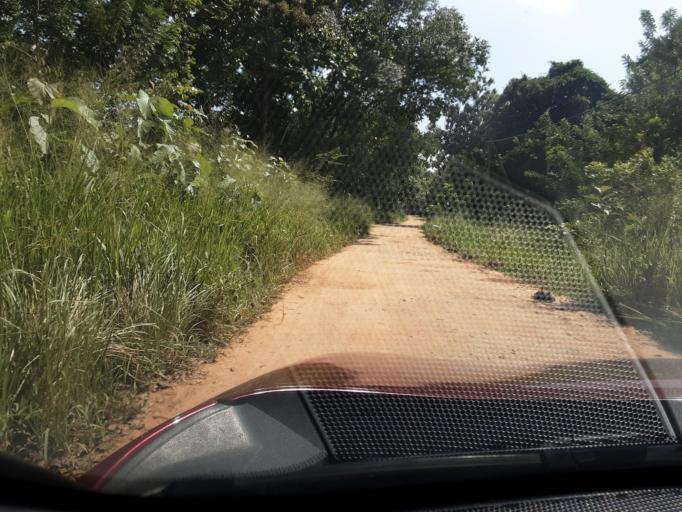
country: LK
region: Central
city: Sigiriya
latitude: 8.0026
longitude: 80.7472
